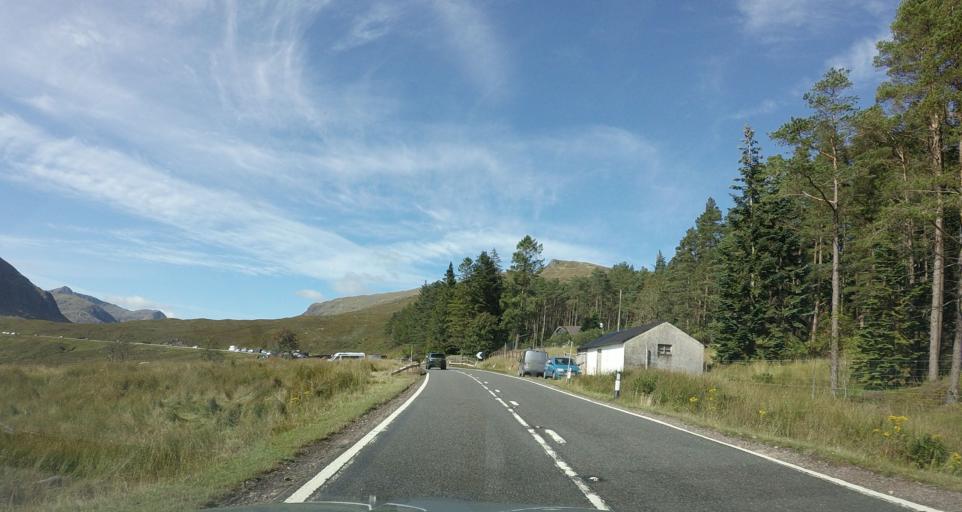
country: GB
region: Scotland
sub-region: Highland
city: Spean Bridge
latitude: 56.6620
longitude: -4.8962
